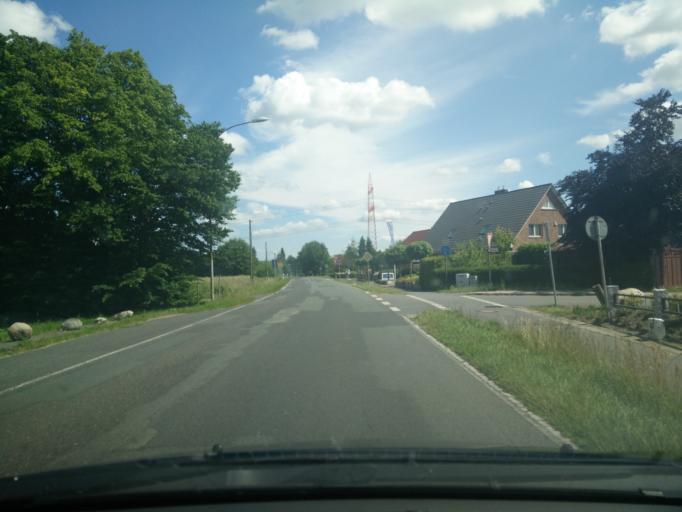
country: DE
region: Schleswig-Holstein
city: Prisdorf
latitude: 53.6833
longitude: 9.7334
